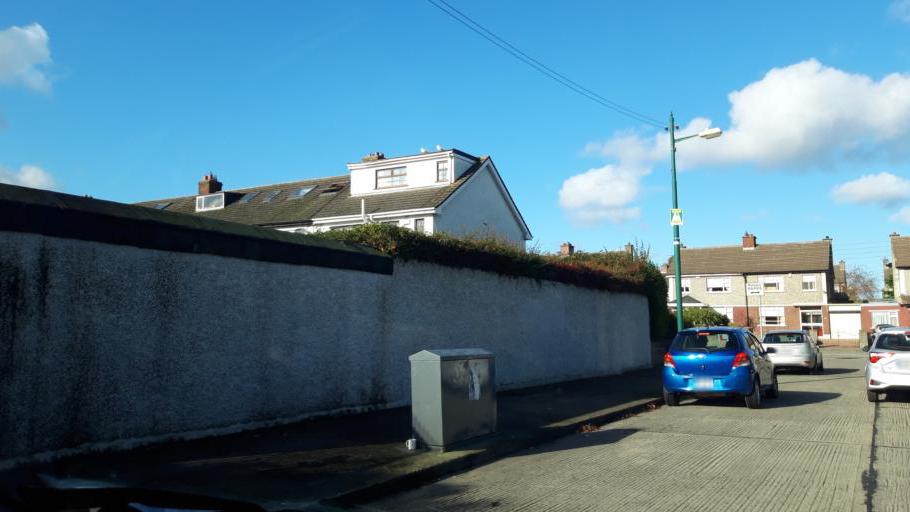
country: IE
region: Leinster
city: Raheny
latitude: 53.3893
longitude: -6.1865
